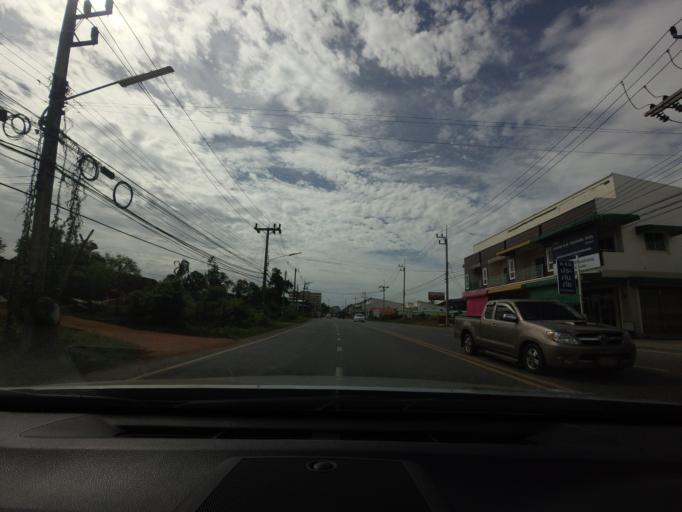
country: TH
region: Songkhla
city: Khlong Hoi Khong
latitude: 6.9448
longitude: 100.4143
